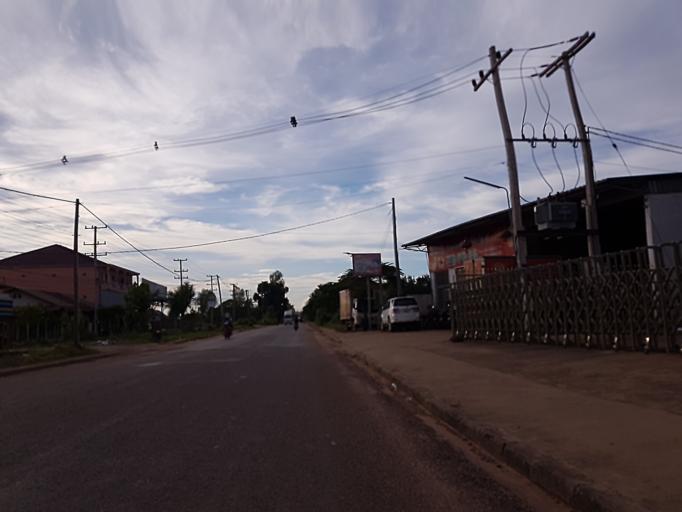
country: TH
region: Nong Khai
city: Si Chiang Mai
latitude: 17.9970
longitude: 102.5660
